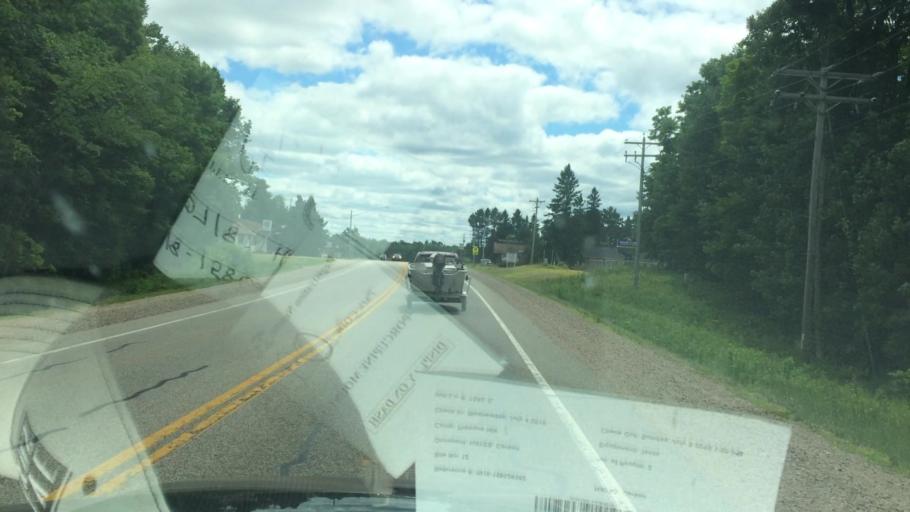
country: US
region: Wisconsin
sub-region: Vilas County
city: Eagle River
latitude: 45.7913
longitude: -89.3209
